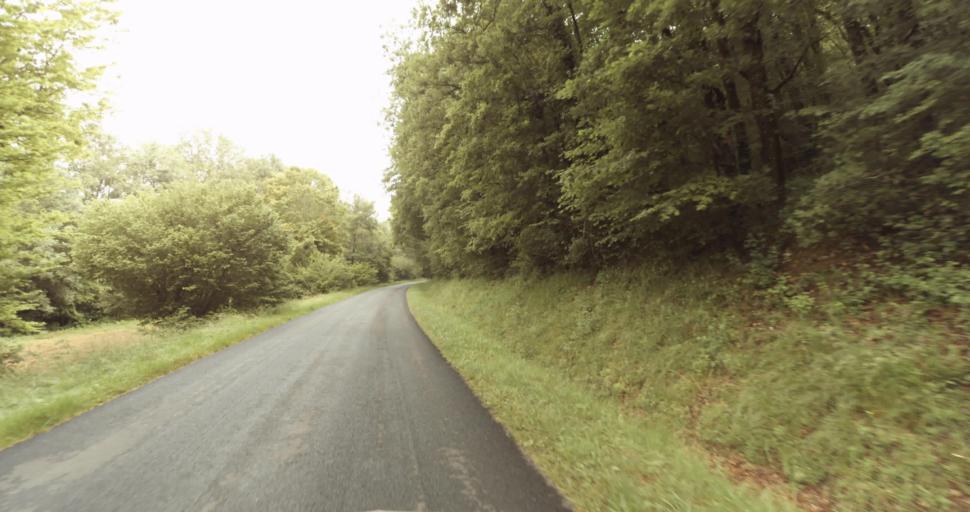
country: FR
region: Aquitaine
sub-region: Departement de la Dordogne
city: Lalinde
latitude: 44.8641
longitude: 0.7738
